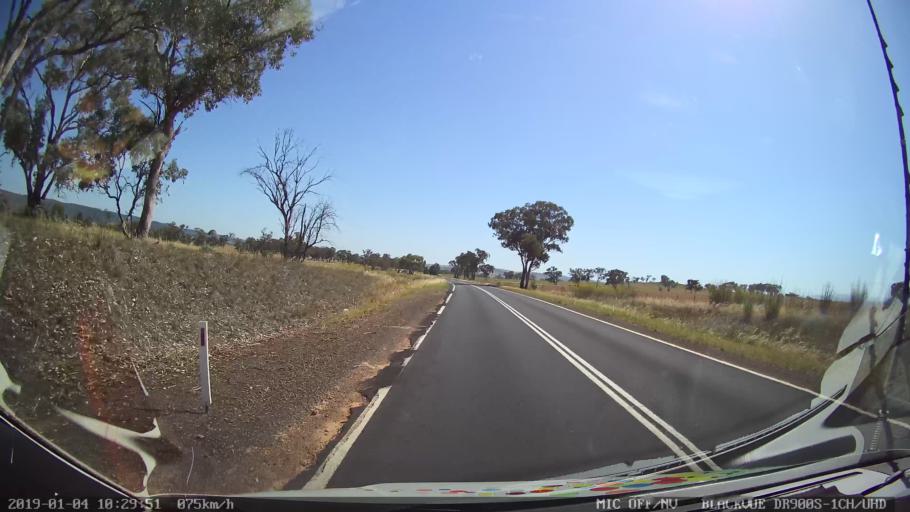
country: AU
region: New South Wales
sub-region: Cabonne
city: Canowindra
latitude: -33.3522
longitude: 148.6241
